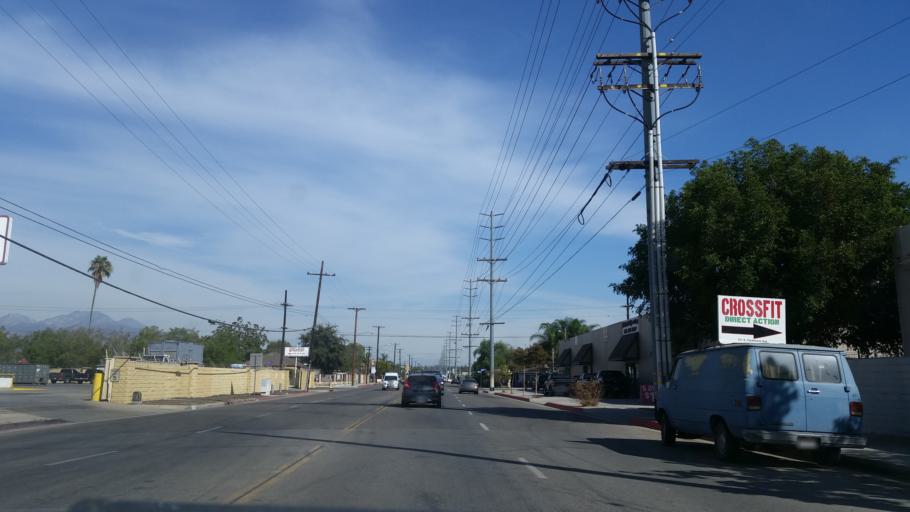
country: US
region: California
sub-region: Los Angeles County
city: Irwindale
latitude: 34.1143
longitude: -117.9222
